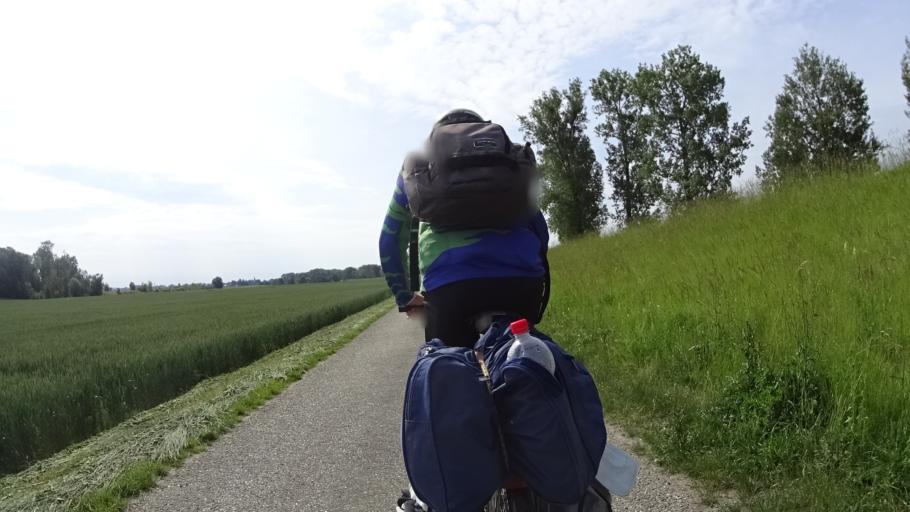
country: DE
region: Bavaria
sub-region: Lower Bavaria
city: Mariaposching
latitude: 48.8353
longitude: 12.7794
